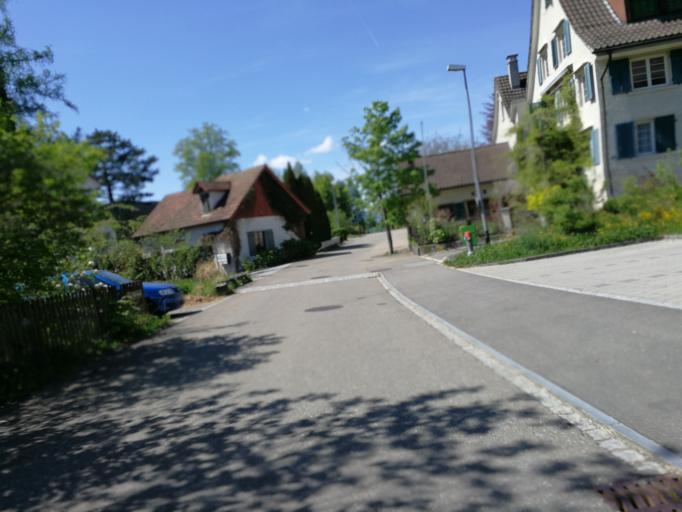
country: CH
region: Zurich
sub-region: Bezirk Meilen
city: Maennedorf / Dorfkern
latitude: 47.2593
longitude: 8.6864
